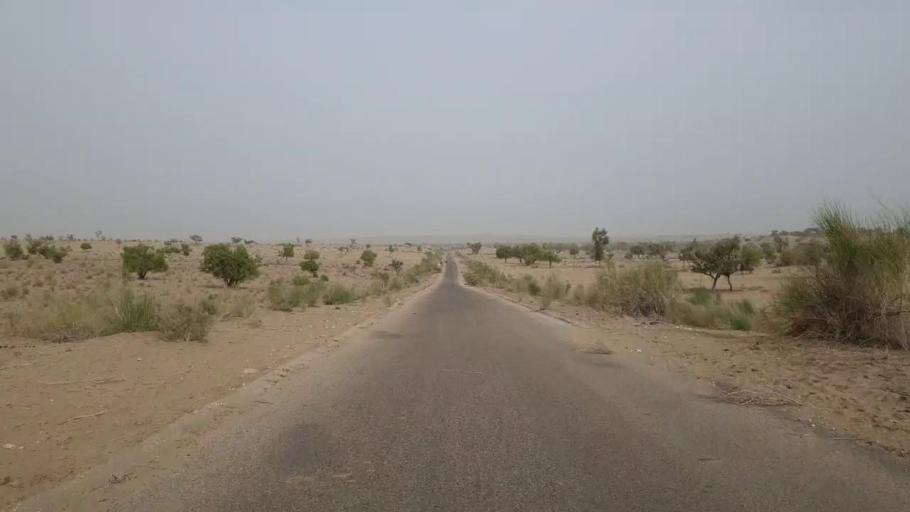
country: PK
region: Sindh
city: Islamkot
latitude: 24.5546
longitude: 70.3498
